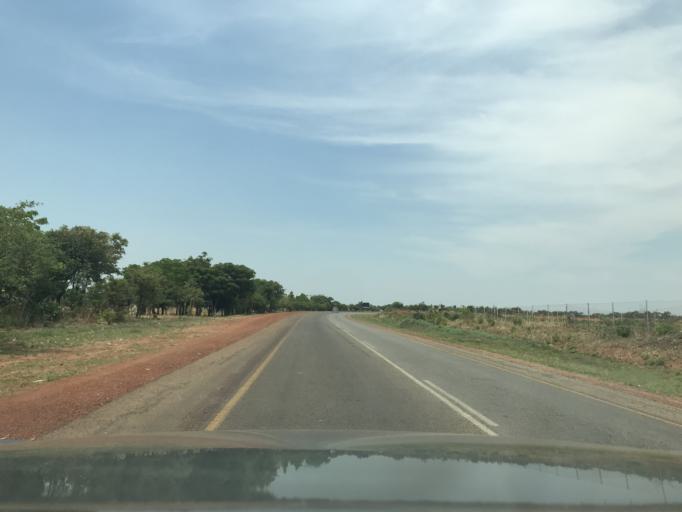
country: ZM
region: Northern
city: Kasama
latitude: -10.2201
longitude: 31.1371
